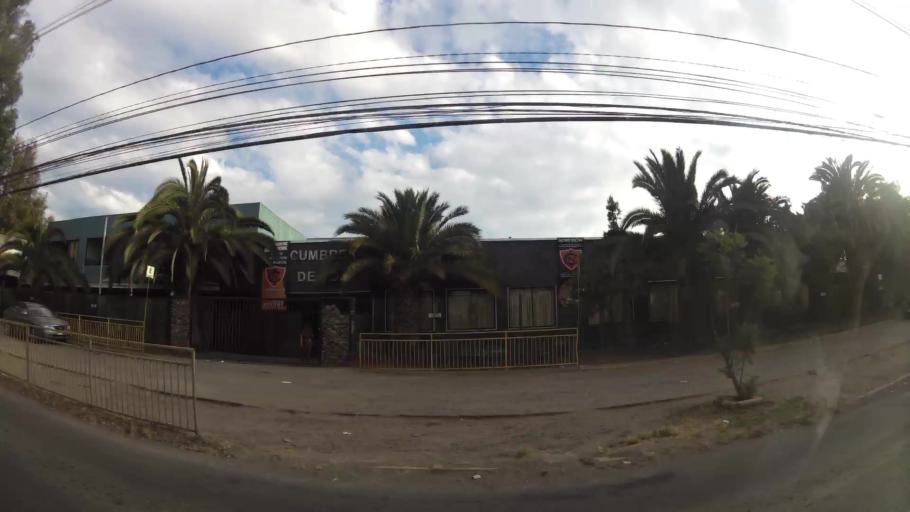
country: CL
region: Santiago Metropolitan
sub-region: Provincia de Maipo
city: San Bernardo
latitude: -33.6395
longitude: -70.6775
